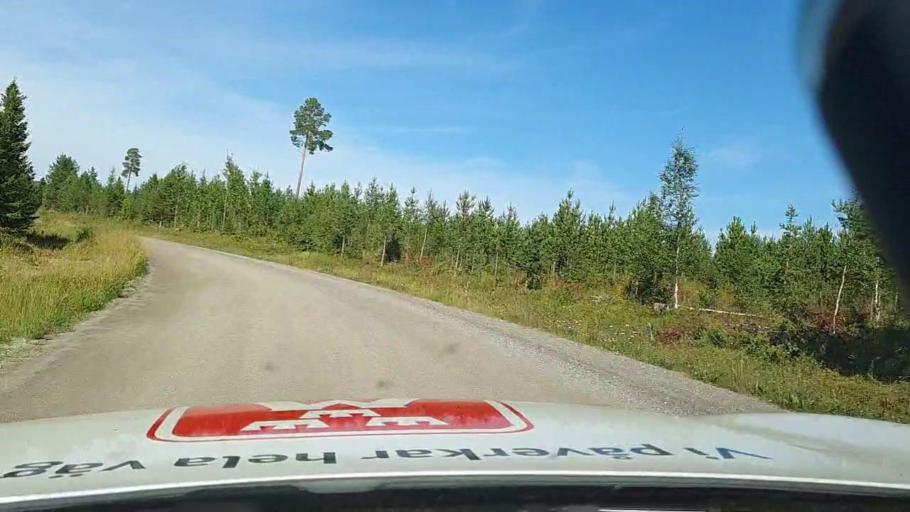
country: SE
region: Jaemtland
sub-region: Stroemsunds Kommun
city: Stroemsund
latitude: 63.6874
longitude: 15.3885
